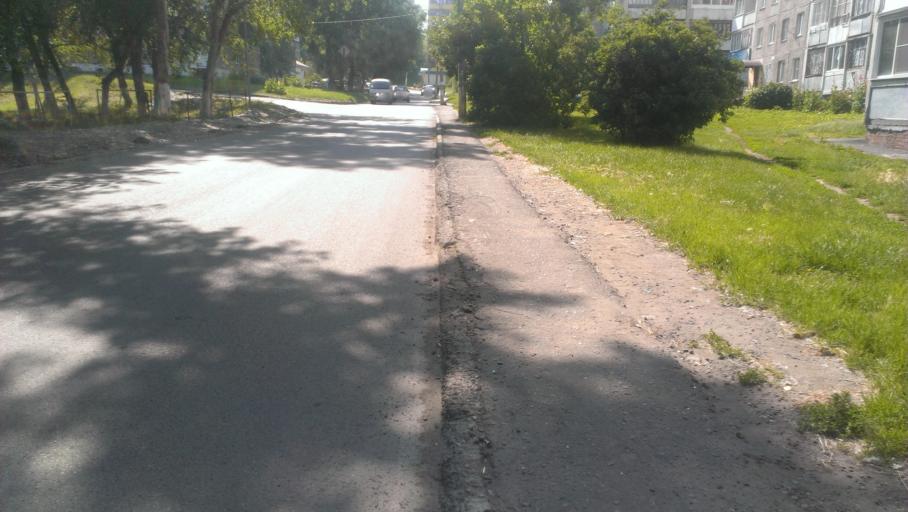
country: RU
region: Altai Krai
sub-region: Gorod Barnaulskiy
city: Barnaul
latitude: 53.3834
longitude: 83.6797
